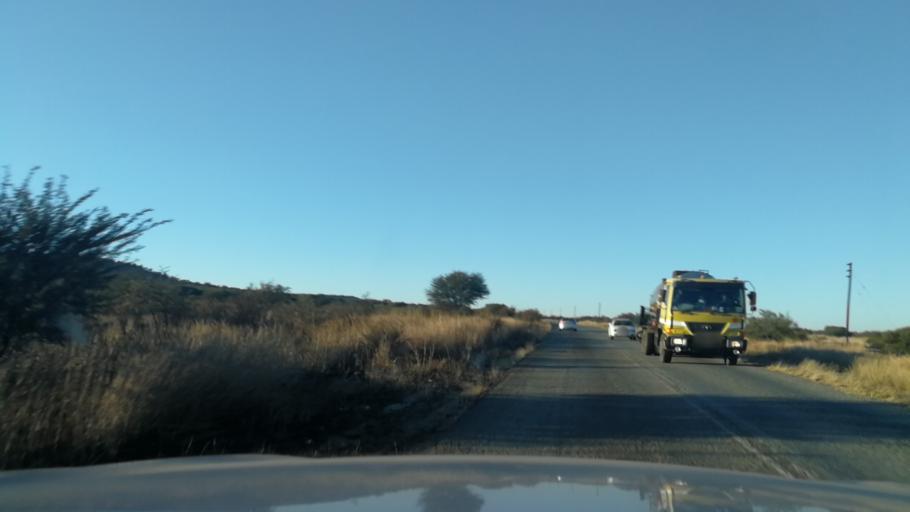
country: ZA
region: North-West
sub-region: Bojanala Platinum District Municipality
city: Koster
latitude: -25.7367
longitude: 26.7482
